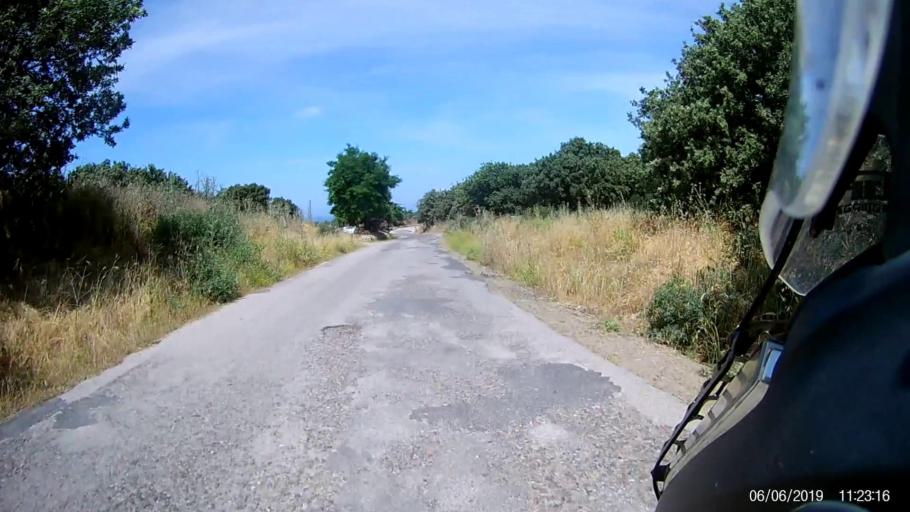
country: TR
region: Canakkale
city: Gulpinar
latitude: 39.6130
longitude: 26.1785
